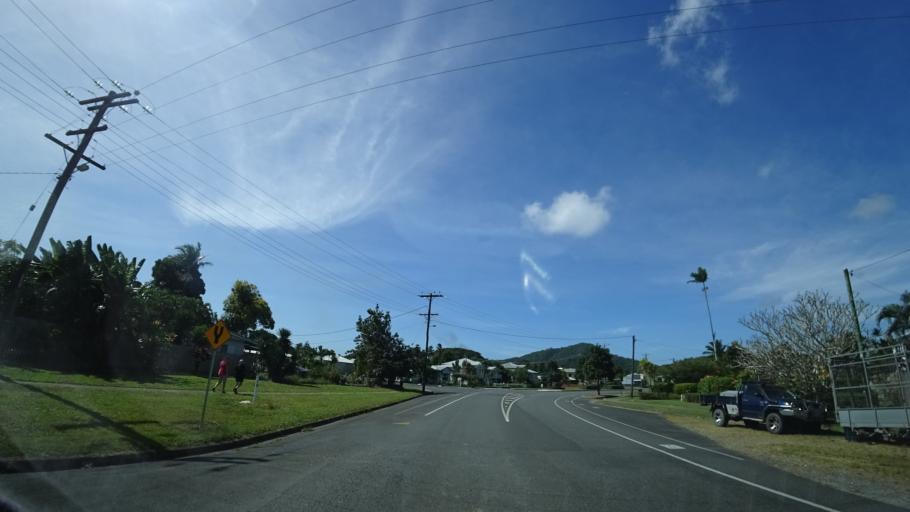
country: AU
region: Queensland
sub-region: Cairns
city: Port Douglas
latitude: -16.4639
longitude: 145.3700
